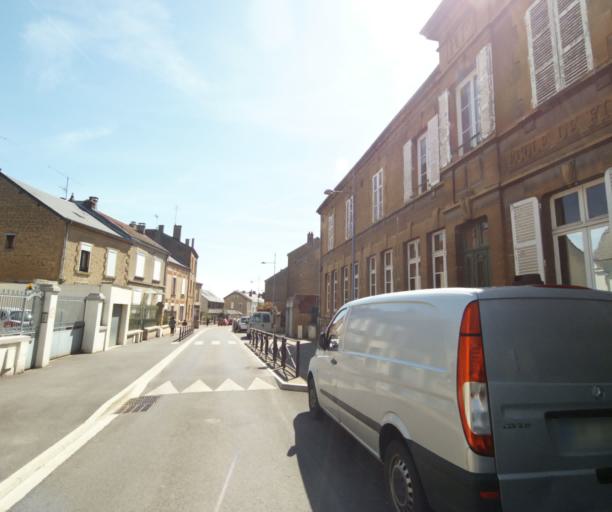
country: FR
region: Champagne-Ardenne
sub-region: Departement des Ardennes
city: Charleville-Mezieres
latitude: 49.7538
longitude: 4.7281
